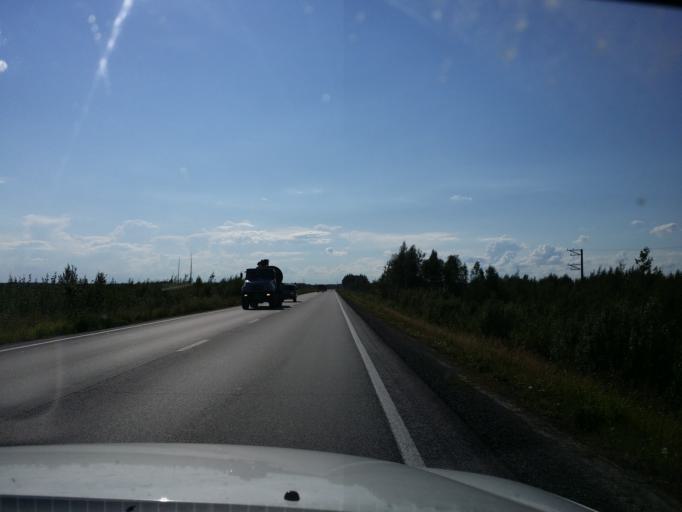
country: RU
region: Khanty-Mansiyskiy Avtonomnyy Okrug
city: Lokosovo
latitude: 61.3941
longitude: 74.8897
